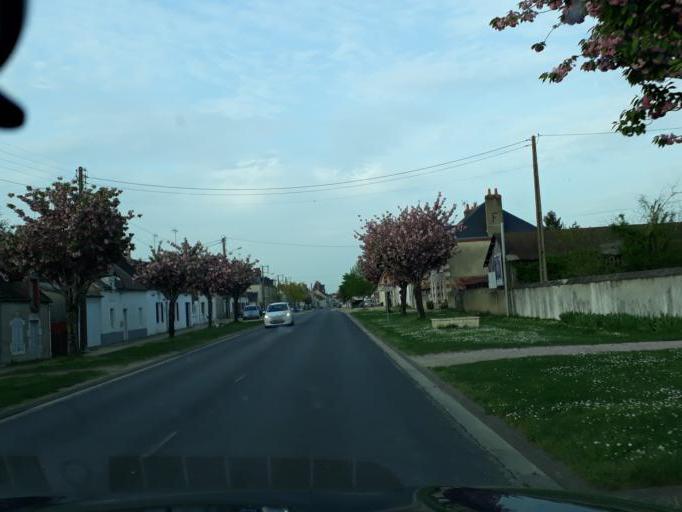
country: FR
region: Centre
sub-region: Departement du Loir-et-Cher
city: Saint-Laurent-Nouan
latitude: 47.7143
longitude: 1.6069
